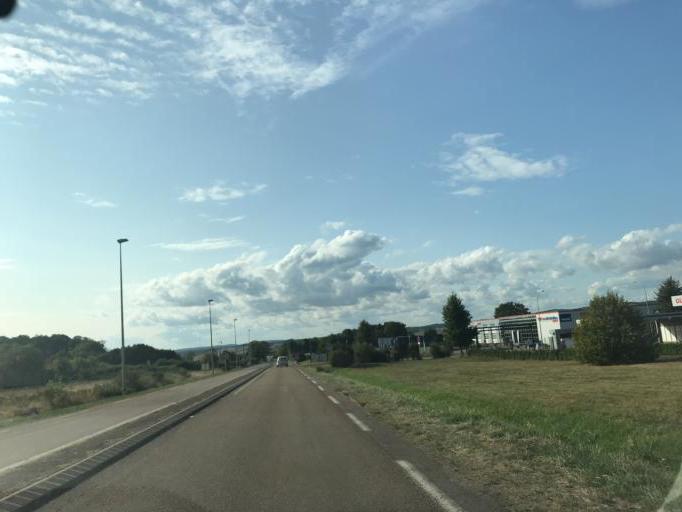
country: FR
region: Bourgogne
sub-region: Departement de l'Yonne
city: Avallon
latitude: 47.4975
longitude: 3.8969
